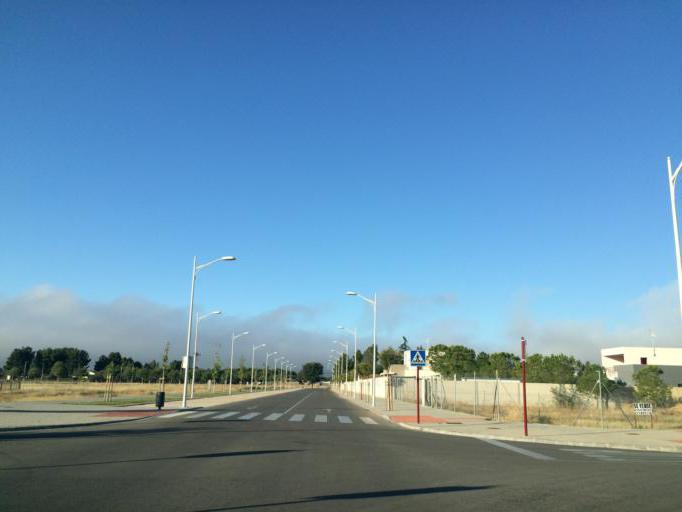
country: ES
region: Castille-La Mancha
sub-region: Provincia de Albacete
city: Albacete
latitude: 39.0042
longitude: -1.8778
